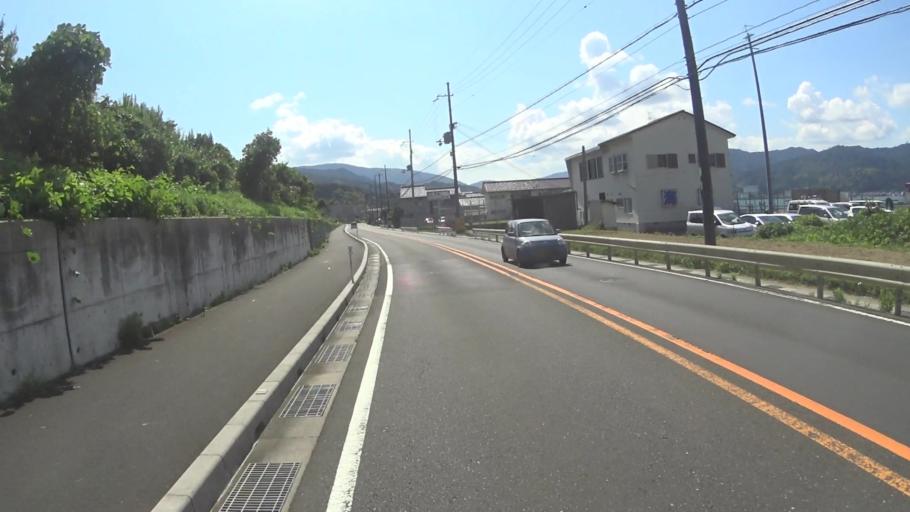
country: JP
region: Kyoto
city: Miyazu
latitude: 35.5471
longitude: 135.2112
